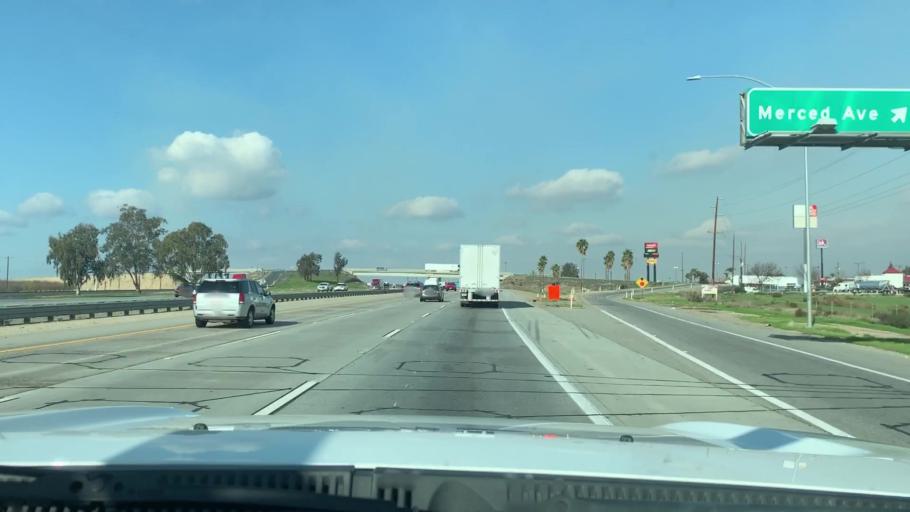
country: US
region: California
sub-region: Kern County
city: Shafter
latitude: 35.5267
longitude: -119.1885
